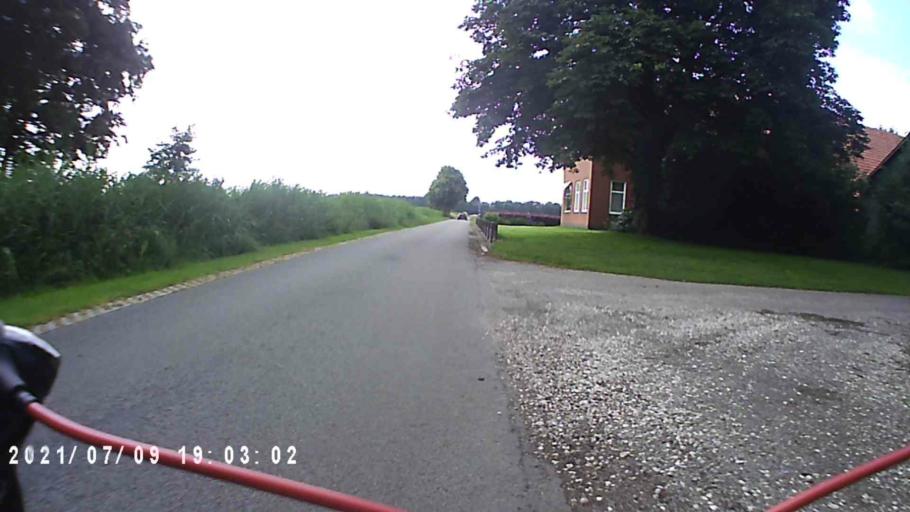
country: NL
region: Groningen
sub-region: Gemeente Veendam
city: Veendam
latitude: 53.0472
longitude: 6.8918
